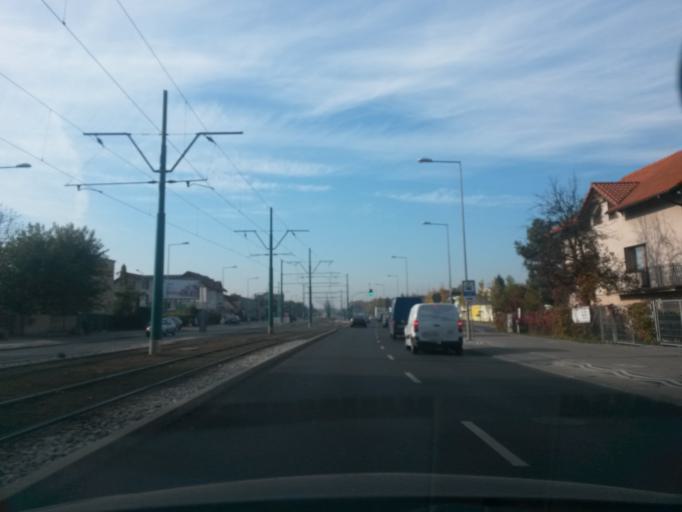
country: PL
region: Greater Poland Voivodeship
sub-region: Powiat poznanski
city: Plewiska
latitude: 52.3872
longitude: 16.8457
